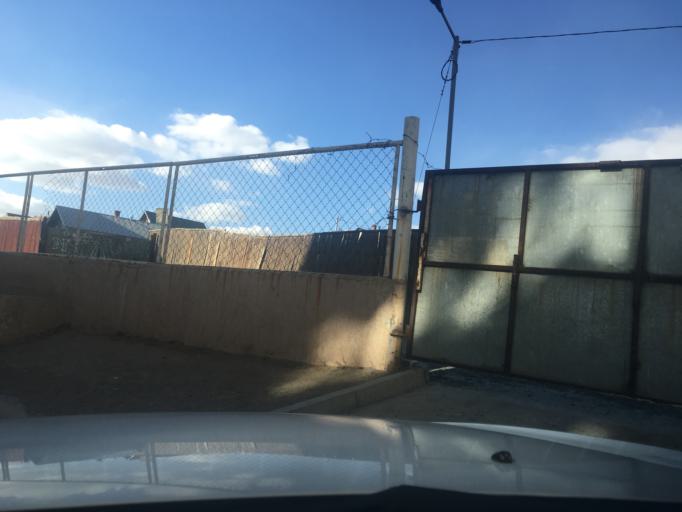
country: MN
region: Ulaanbaatar
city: Ulaanbaatar
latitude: 47.9258
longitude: 106.8074
